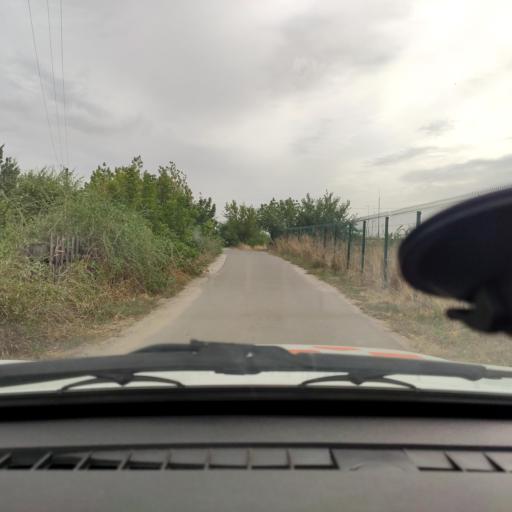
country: RU
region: Lipetsk
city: Khlevnoye
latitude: 52.0056
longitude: 39.1123
